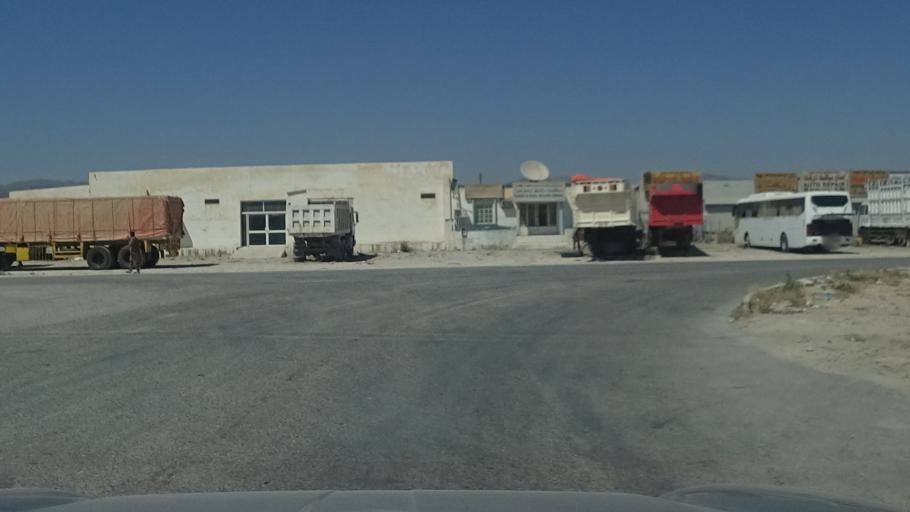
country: OM
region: Zufar
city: Salalah
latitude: 17.0279
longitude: 54.0434
